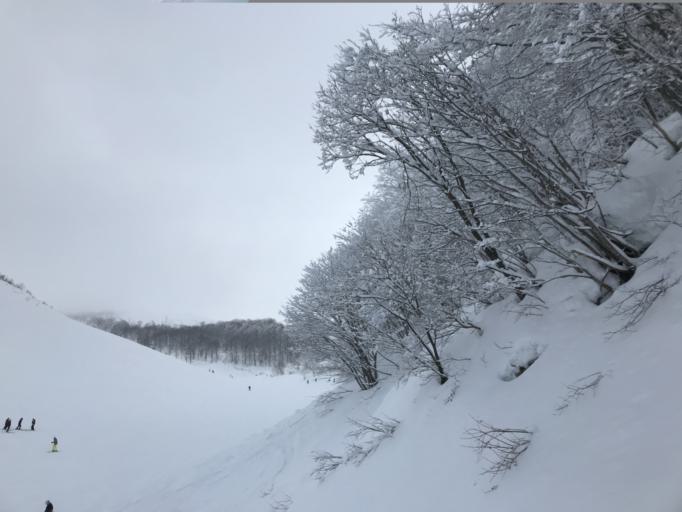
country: JP
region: Nagano
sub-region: Kitaazumi Gun
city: Hakuba
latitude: 36.7076
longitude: 137.8161
